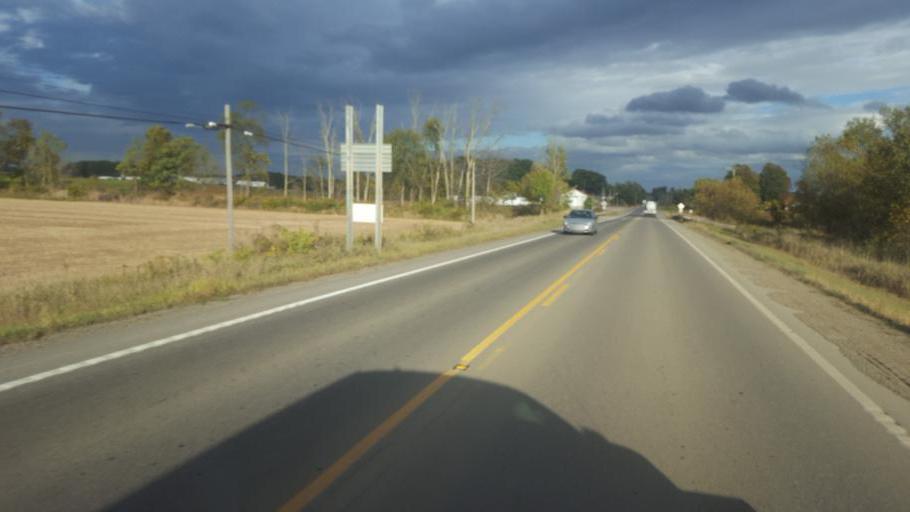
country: US
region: Ohio
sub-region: Ashland County
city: Ashland
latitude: 40.8573
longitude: -82.2475
